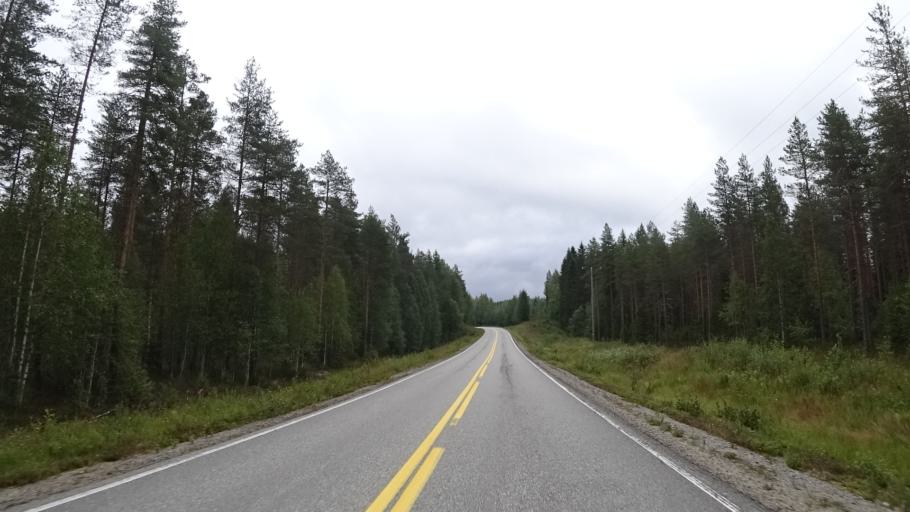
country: FI
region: North Karelia
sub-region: Joensuu
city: Ilomantsi
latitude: 63.2598
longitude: 30.6635
